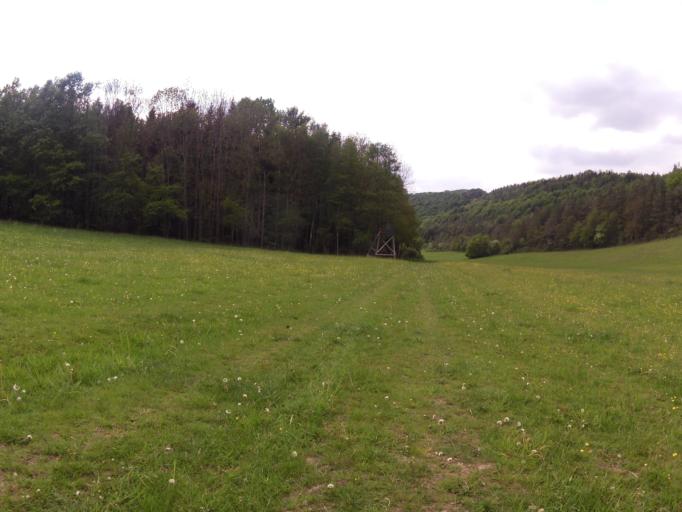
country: DE
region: Thuringia
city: Seebach
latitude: 50.9608
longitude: 10.4333
